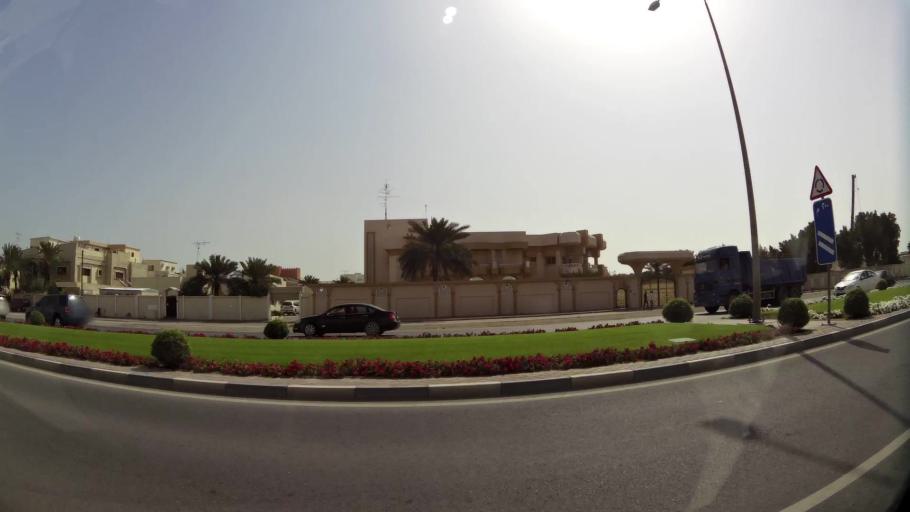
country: QA
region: Baladiyat ad Dawhah
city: Doha
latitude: 25.2483
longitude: 51.5242
